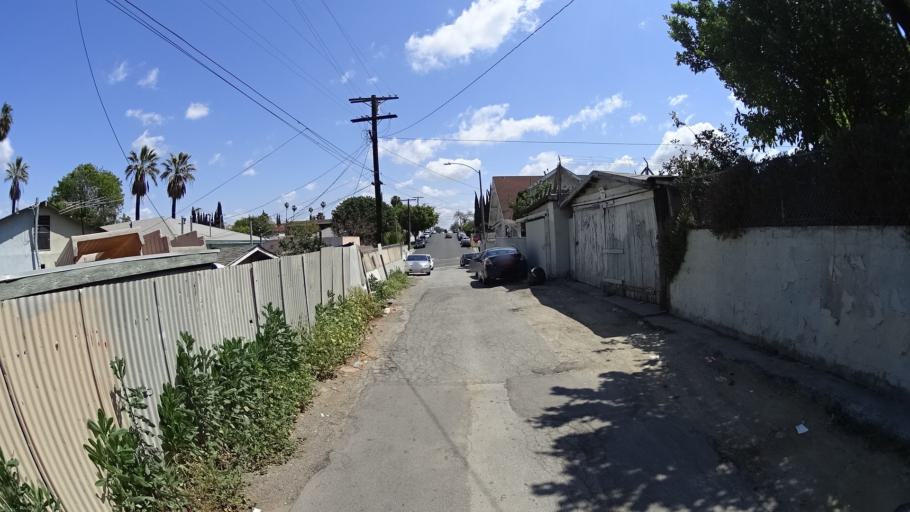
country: US
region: California
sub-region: Los Angeles County
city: Boyle Heights
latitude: 34.0518
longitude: -118.2101
